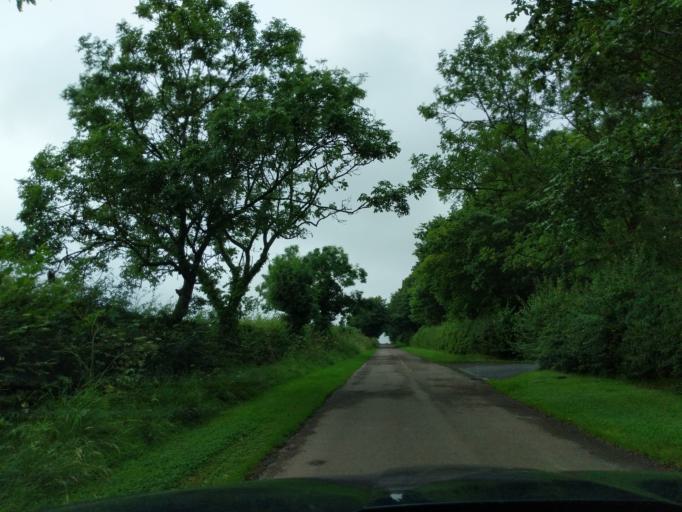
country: GB
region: England
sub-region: Northumberland
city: Ford
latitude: 55.6801
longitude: -2.1208
